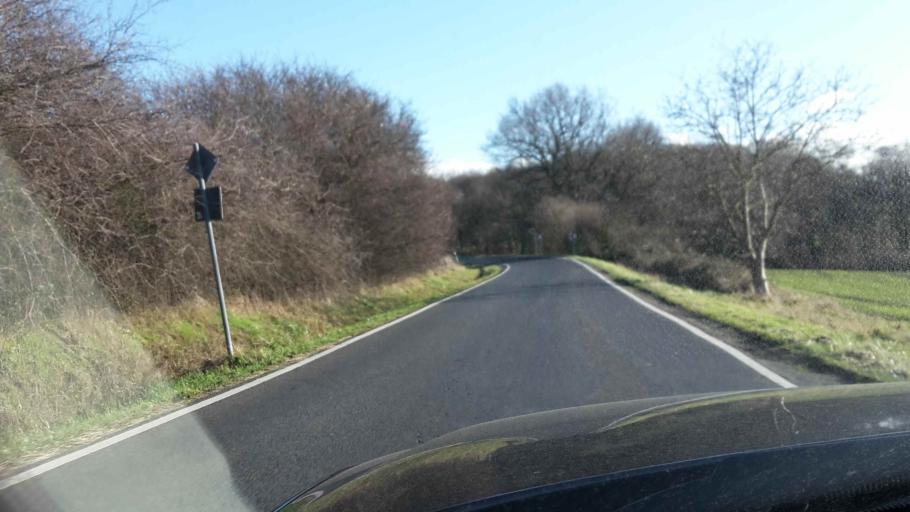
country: DE
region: North Rhine-Westphalia
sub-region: Regierungsbezirk Koln
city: Hennef
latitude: 50.7109
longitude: 7.2874
